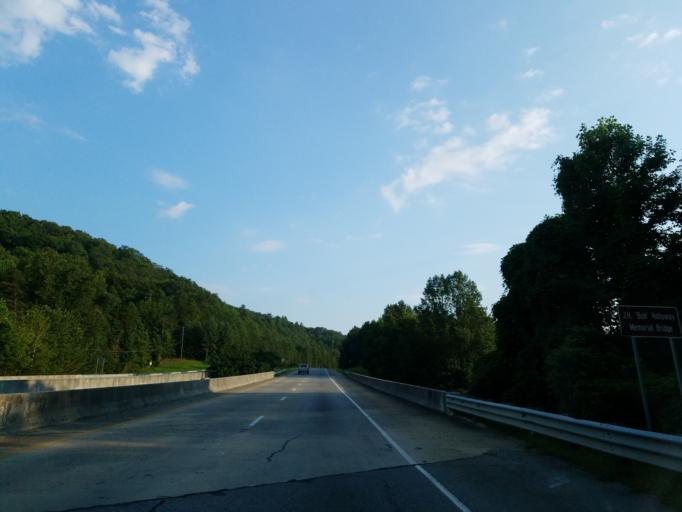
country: US
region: Georgia
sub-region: Fannin County
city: Blue Ridge
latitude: 34.7864
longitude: -84.3876
